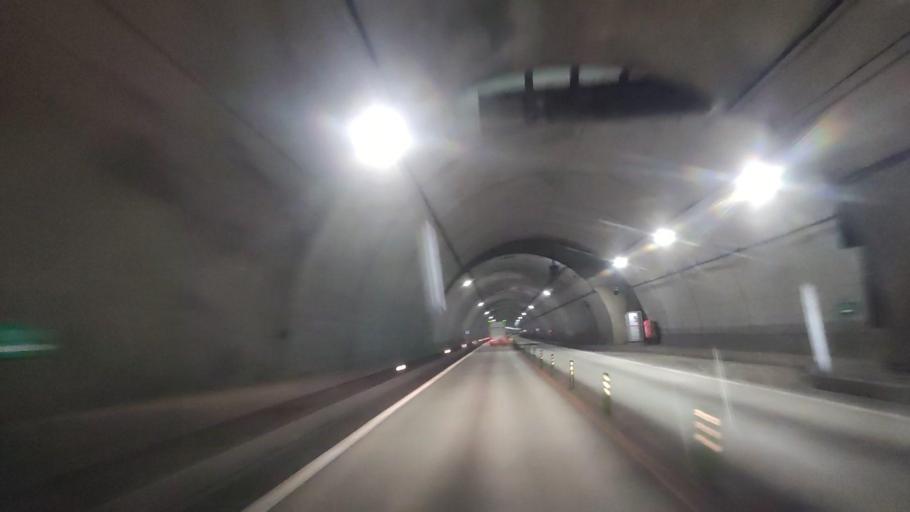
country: JP
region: Ishikawa
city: Nanao
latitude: 37.0217
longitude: 137.0031
